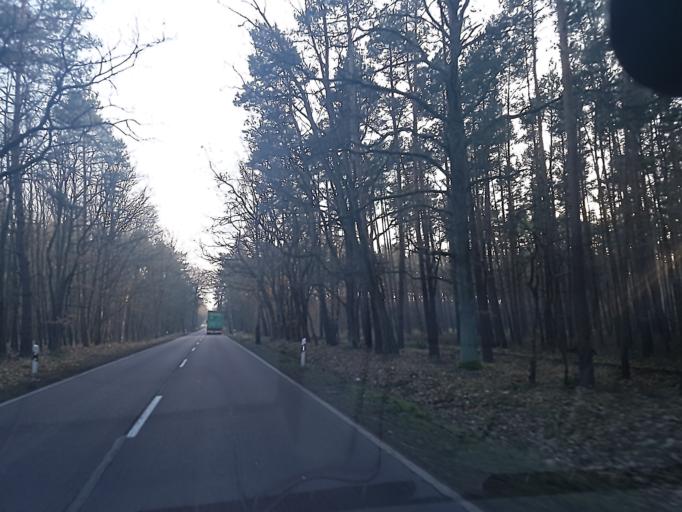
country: DE
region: Saxony-Anhalt
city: Coswig
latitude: 51.9709
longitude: 12.4658
